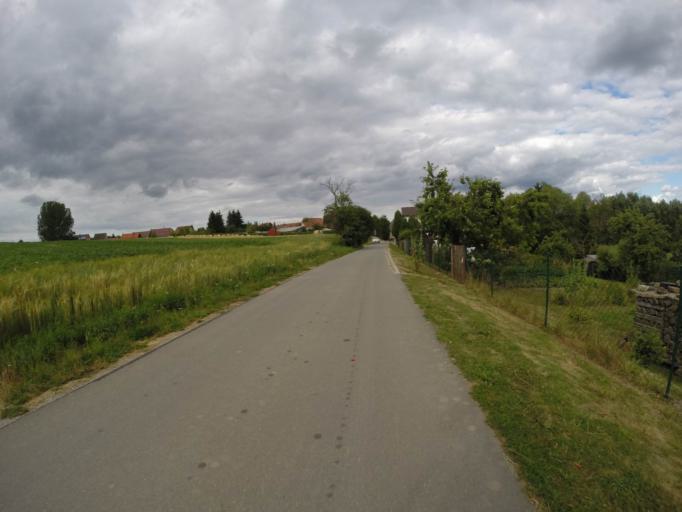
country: DE
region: Thuringia
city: Burgel
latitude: 50.9347
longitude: 11.7465
